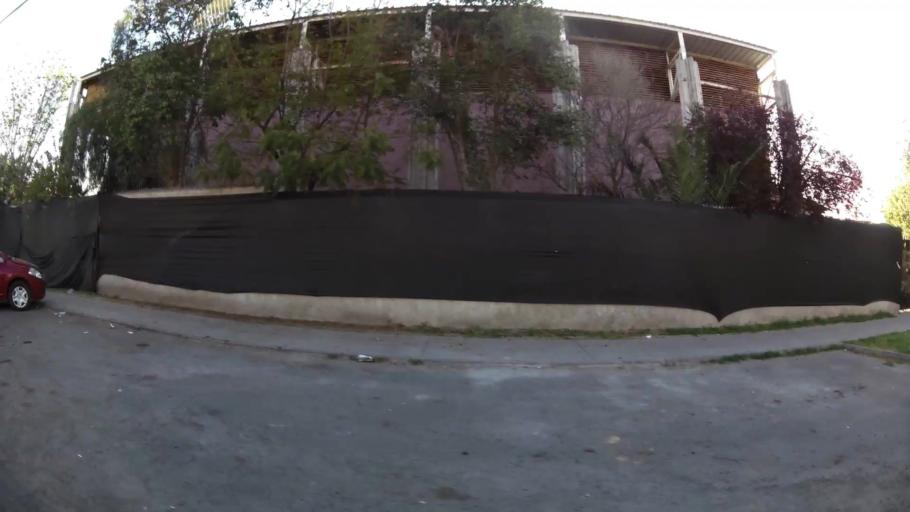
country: CL
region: Santiago Metropolitan
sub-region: Provincia de Cordillera
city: Puente Alto
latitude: -33.6033
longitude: -70.5714
